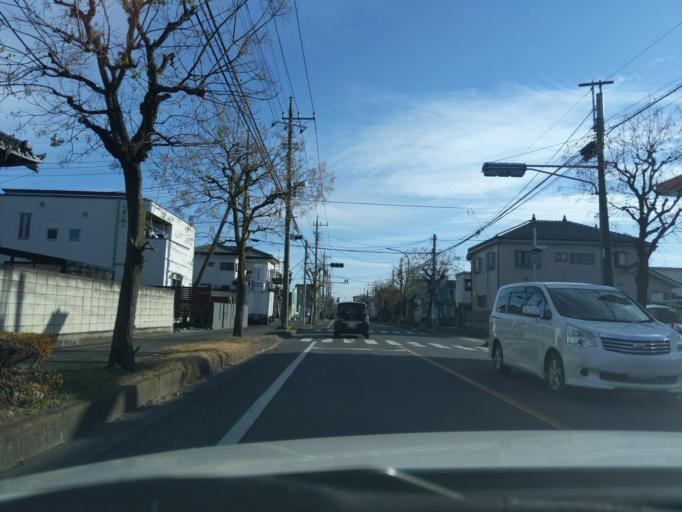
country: JP
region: Saitama
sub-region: Kawaguchi-shi
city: Hatogaya-honcho
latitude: 35.8167
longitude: 139.7479
